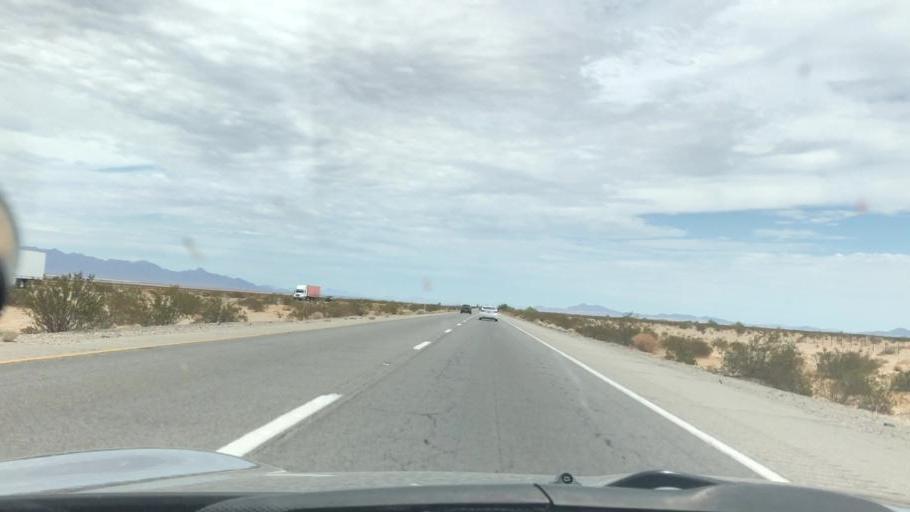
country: US
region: California
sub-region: Riverside County
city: Mesa Verde
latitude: 33.6425
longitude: -115.1095
